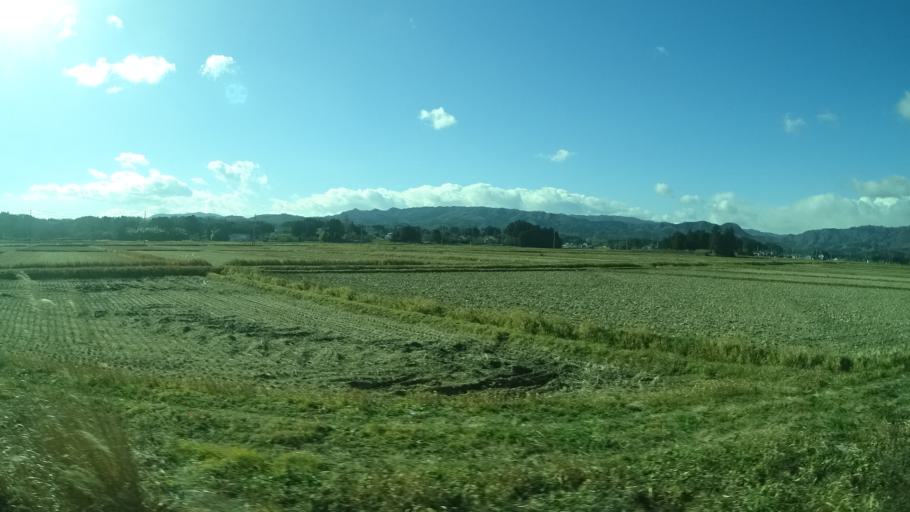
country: JP
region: Miyagi
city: Marumori
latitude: 37.7706
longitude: 140.9218
